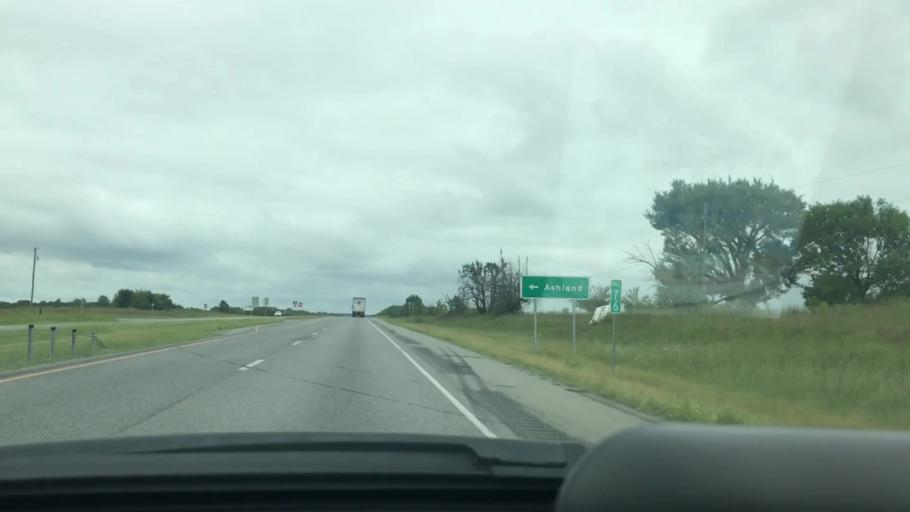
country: US
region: Oklahoma
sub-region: Pittsburg County
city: McAlester
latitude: 34.7519
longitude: -95.8936
